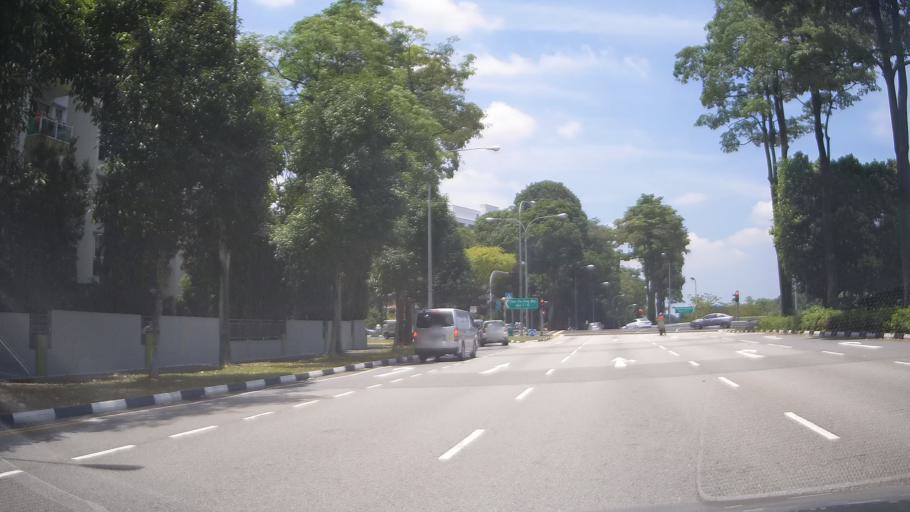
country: MY
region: Johor
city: Johor Bahru
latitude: 1.3867
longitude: 103.7424
